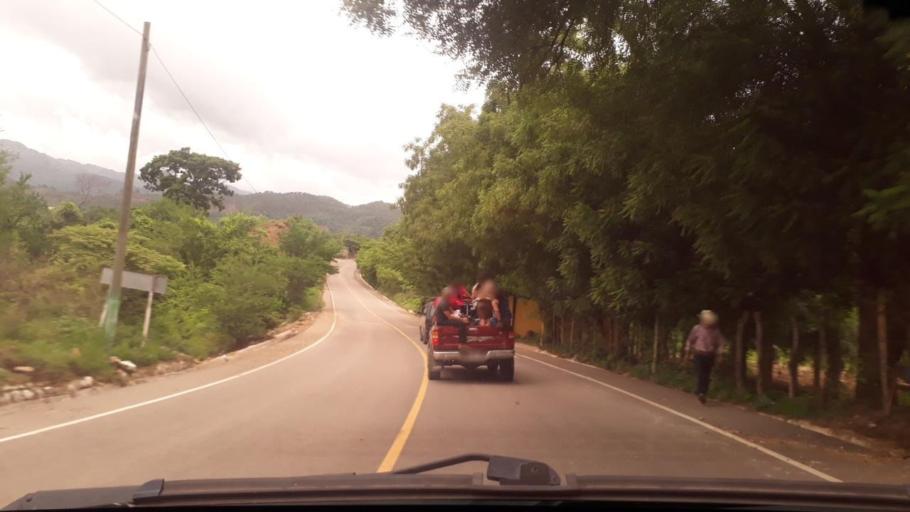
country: GT
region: Chiquimula
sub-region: Municipio de Camotan
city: Camotan
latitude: 14.8207
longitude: -89.3622
